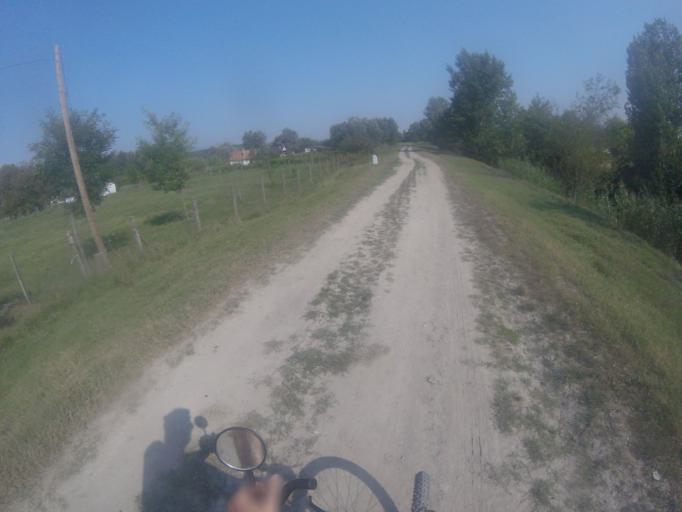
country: HU
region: Bacs-Kiskun
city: Baja
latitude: 46.2090
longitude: 18.9572
